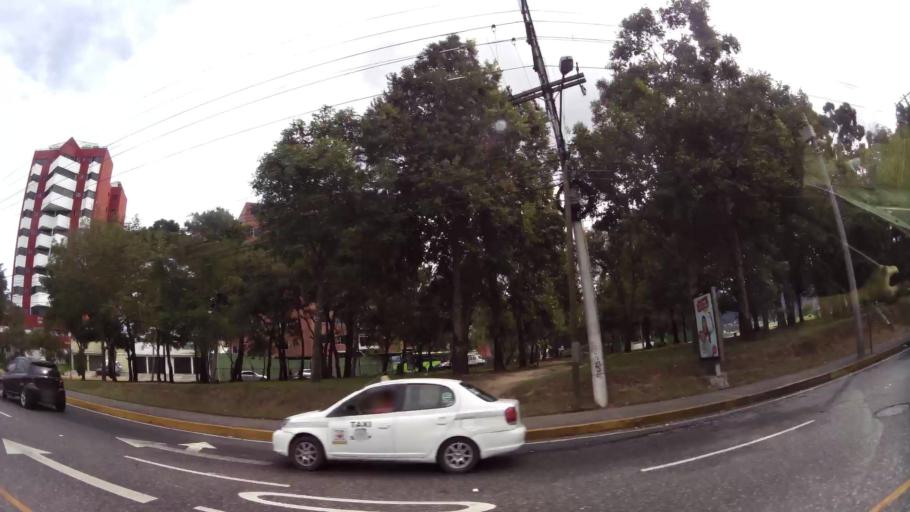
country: GT
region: Guatemala
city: Santa Catarina Pinula
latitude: 14.5701
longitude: -90.5277
